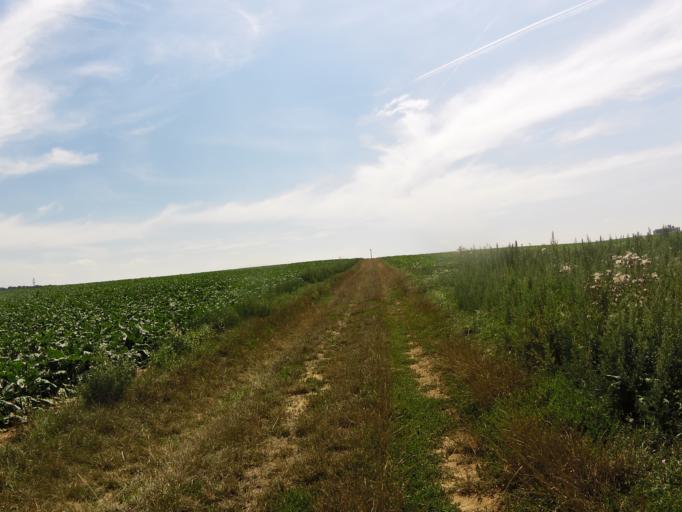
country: DE
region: Bavaria
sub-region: Regierungsbezirk Unterfranken
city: Estenfeld
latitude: 49.8077
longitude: 10.0058
